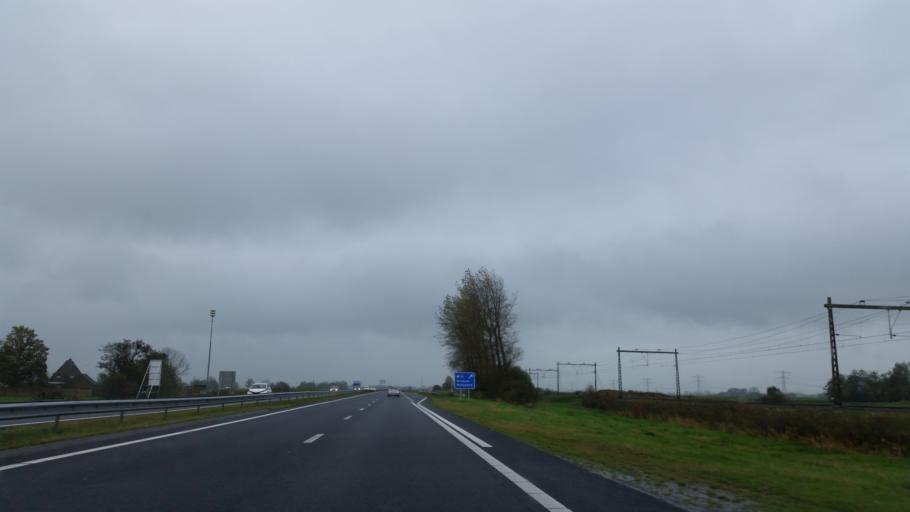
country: NL
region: Friesland
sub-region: Gemeente Leeuwarden
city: Wirdum
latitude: 53.1487
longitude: 5.7937
